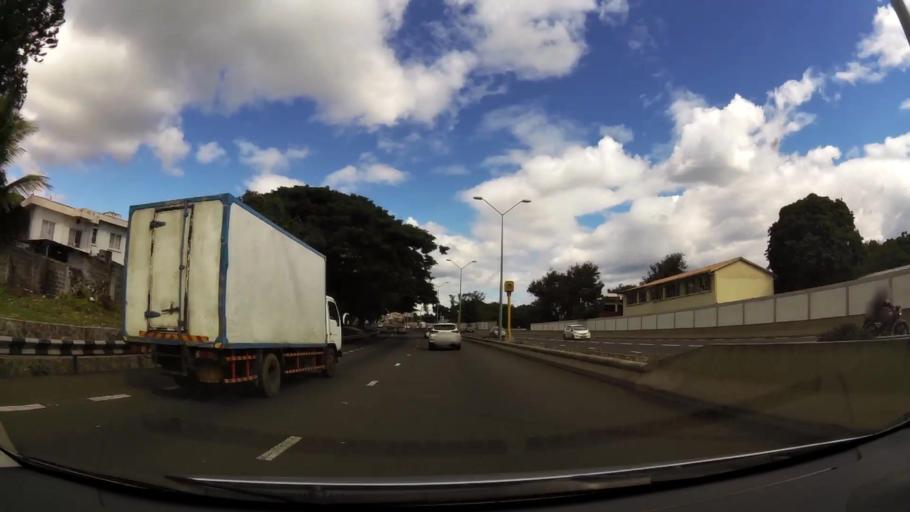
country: MU
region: Port Louis
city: Port Louis
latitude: -20.1647
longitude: 57.4876
